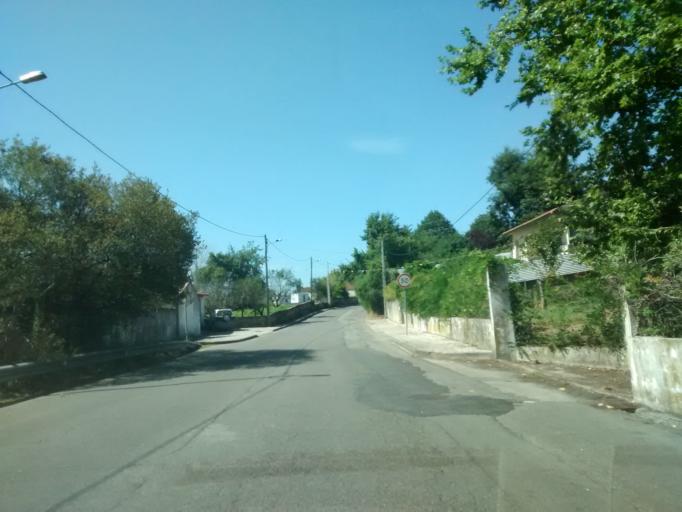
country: PT
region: Coimbra
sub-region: Mira
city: Mira
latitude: 40.4374
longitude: -8.7199
